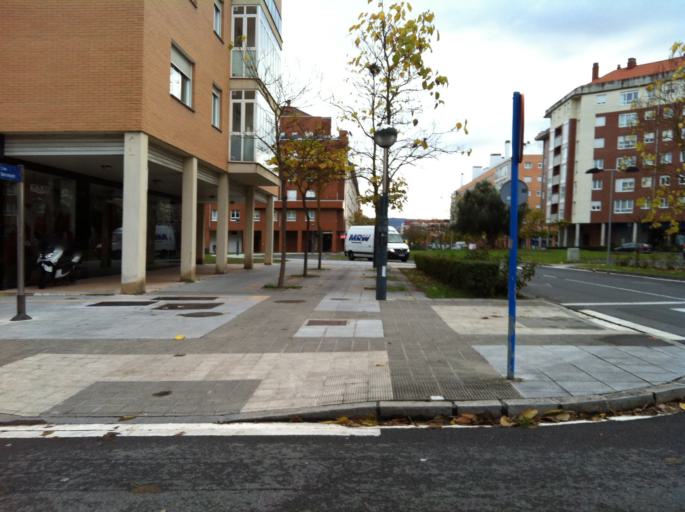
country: ES
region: Basque Country
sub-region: Provincia de Alava
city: Gasteiz / Vitoria
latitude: 42.8673
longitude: -2.6923
